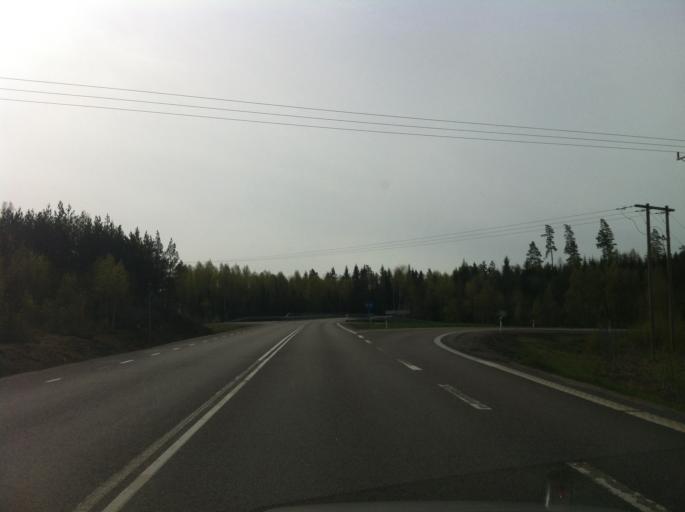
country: SE
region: Vaestra Goetaland
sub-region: Bollebygds Kommun
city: Bollebygd
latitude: 57.6685
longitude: 12.6037
